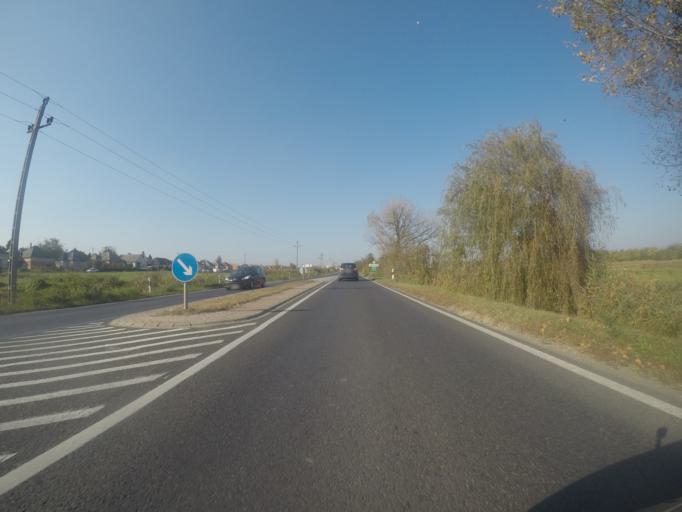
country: HU
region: Tolna
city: Dunafoldvar
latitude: 46.8044
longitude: 18.9159
